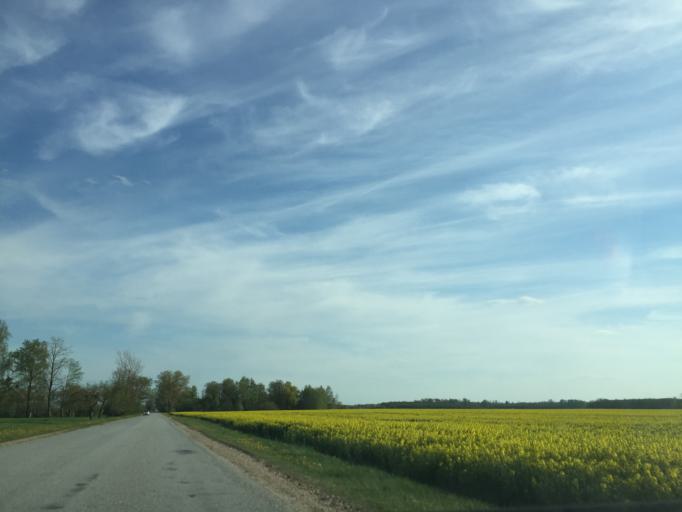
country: LV
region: Bauskas Rajons
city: Bauska
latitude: 56.3604
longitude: 24.2312
